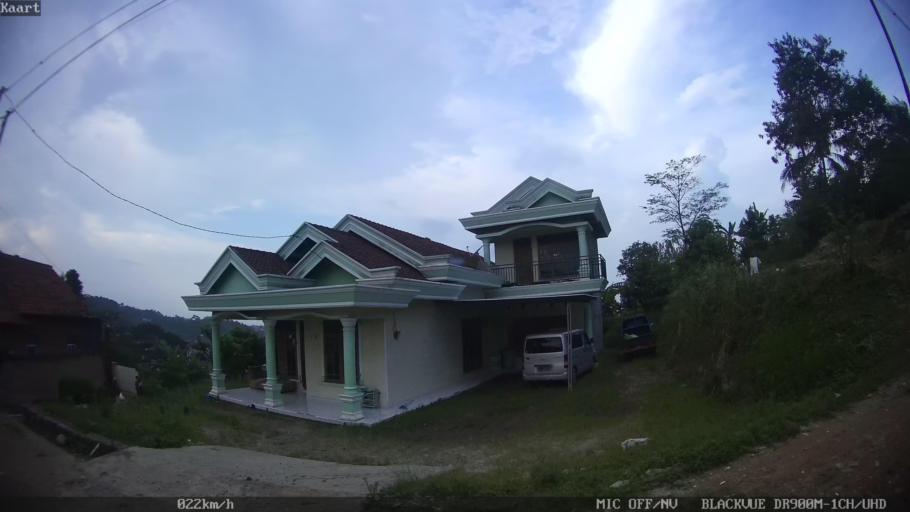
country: ID
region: Lampung
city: Bandarlampung
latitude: -5.4063
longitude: 105.2283
